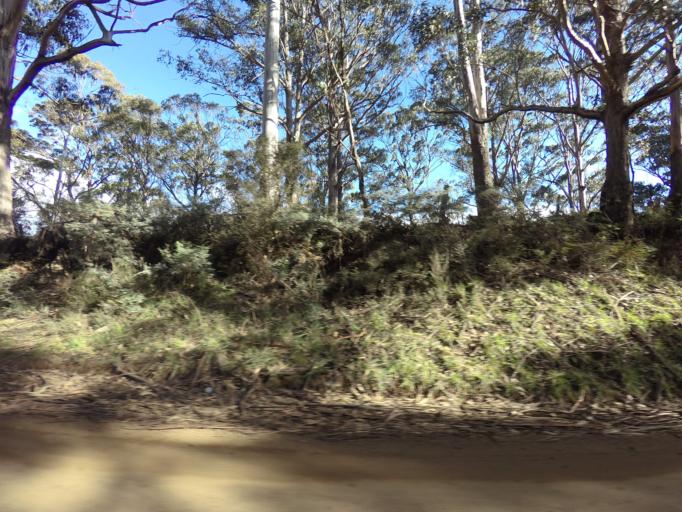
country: AU
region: Tasmania
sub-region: Derwent Valley
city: New Norfolk
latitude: -42.7189
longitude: 147.0345
